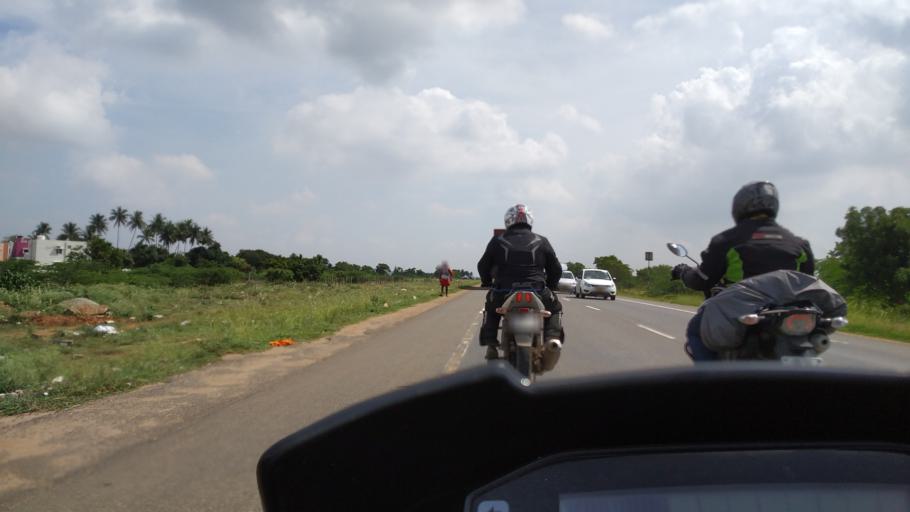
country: IN
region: Tamil Nadu
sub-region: Coimbatore
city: Singanallur
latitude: 10.9713
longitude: 77.0382
